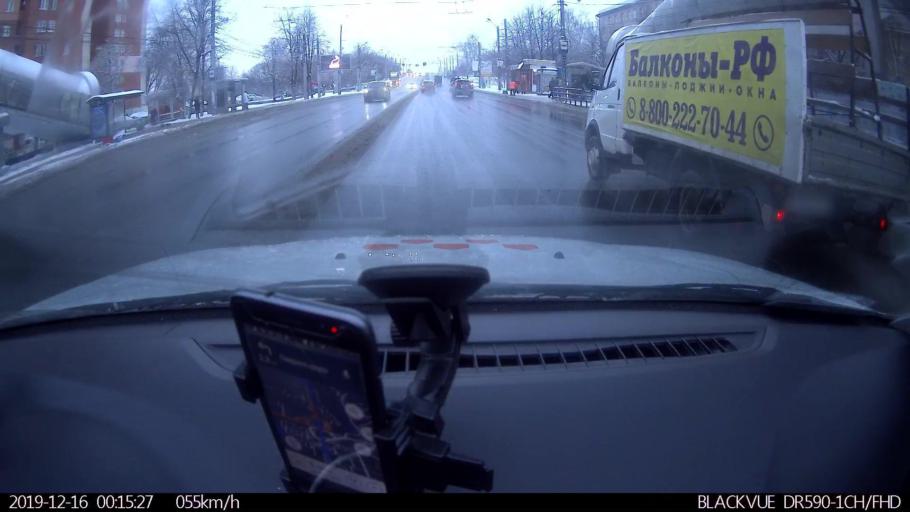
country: RU
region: Nizjnij Novgorod
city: Nizhniy Novgorod
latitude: 56.3150
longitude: 43.8757
